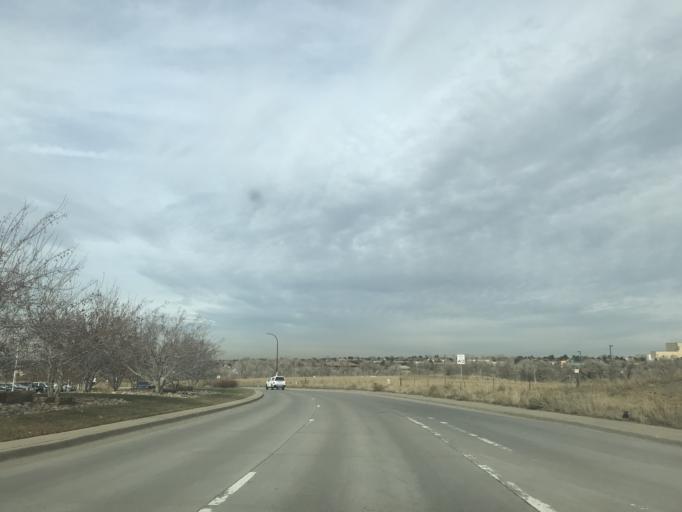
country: US
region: Colorado
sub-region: Douglas County
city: Highlands Ranch
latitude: 39.5608
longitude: -105.0077
